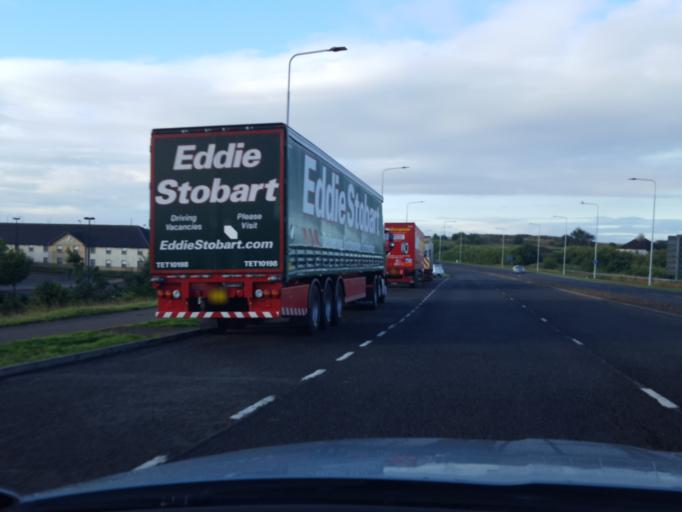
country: GB
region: Scotland
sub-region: Fife
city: Crossgates
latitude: 56.0805
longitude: -3.3992
